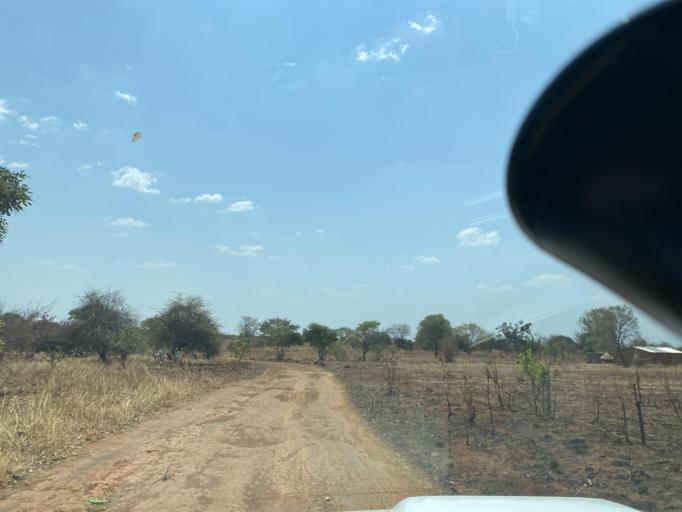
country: ZM
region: Lusaka
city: Lusaka
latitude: -15.4971
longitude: 27.9558
